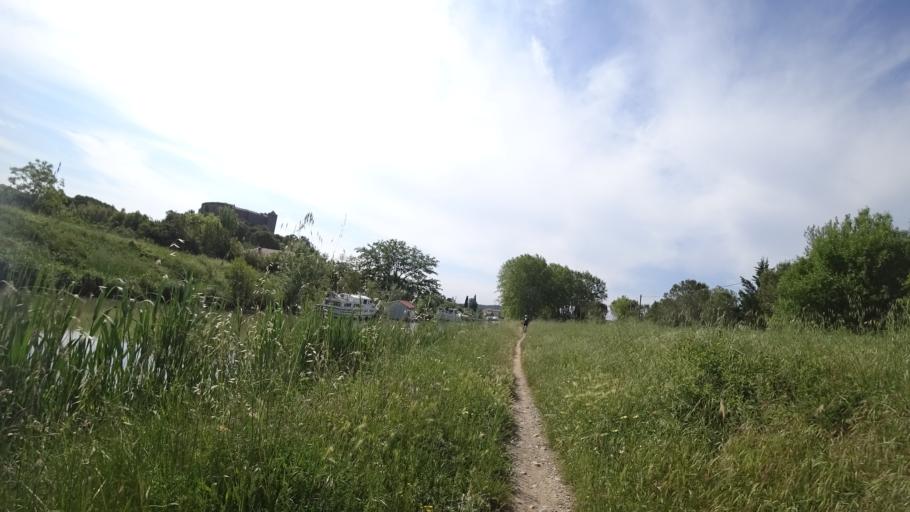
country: FR
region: Languedoc-Roussillon
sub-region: Departement de l'Aude
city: Lezignan-Corbieres
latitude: 43.2436
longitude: 2.7631
